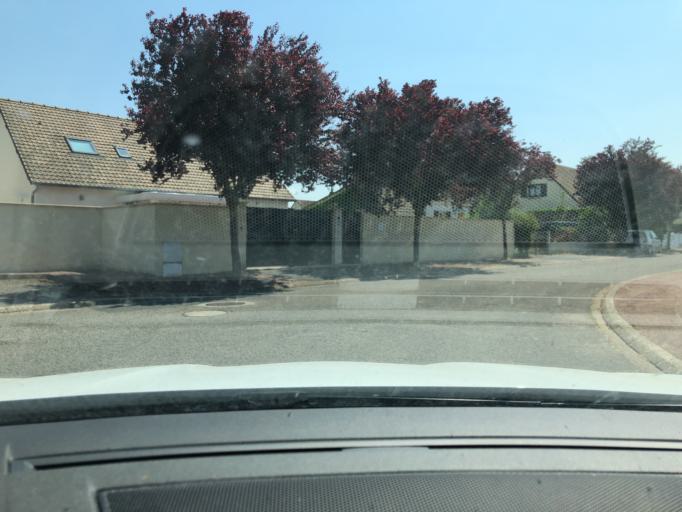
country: FR
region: Lower Normandy
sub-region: Departement du Calvados
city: Lion-sur-Mer
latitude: 49.3034
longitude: -0.3244
